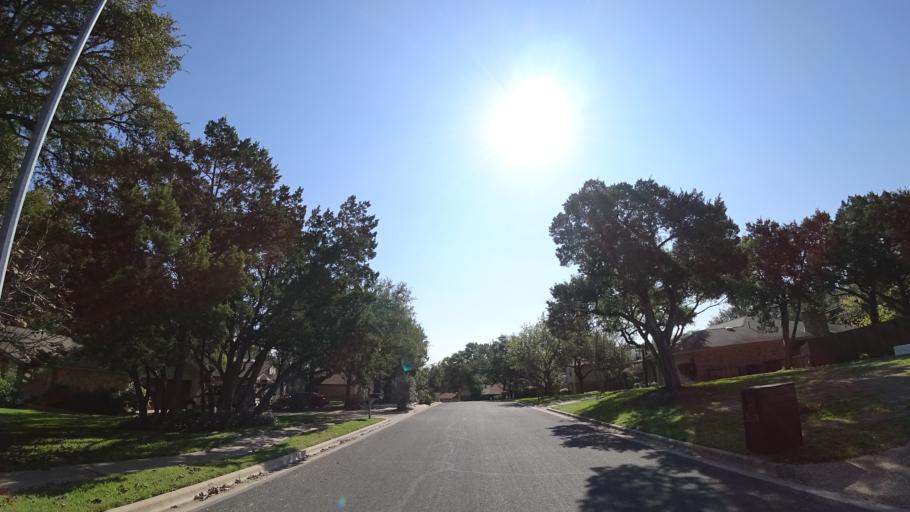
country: US
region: Texas
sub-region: Travis County
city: Rollingwood
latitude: 30.2687
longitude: -97.8121
